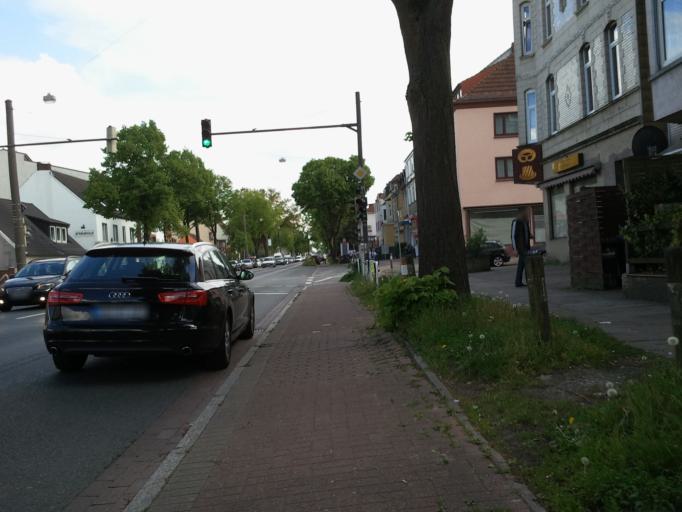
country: DE
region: Lower Saxony
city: Ritterhude
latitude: 53.1251
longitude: 8.7486
